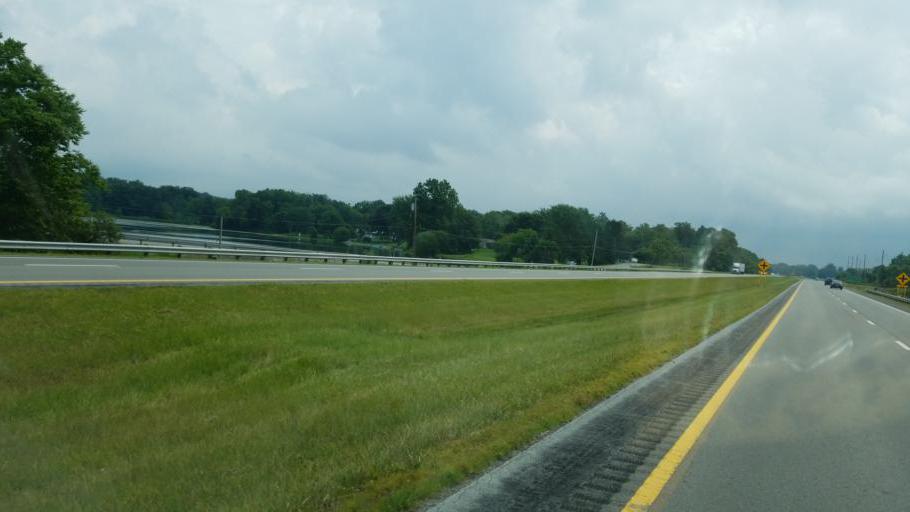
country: US
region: Ohio
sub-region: Logan County
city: Bellefontaine
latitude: 40.4151
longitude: -83.7935
